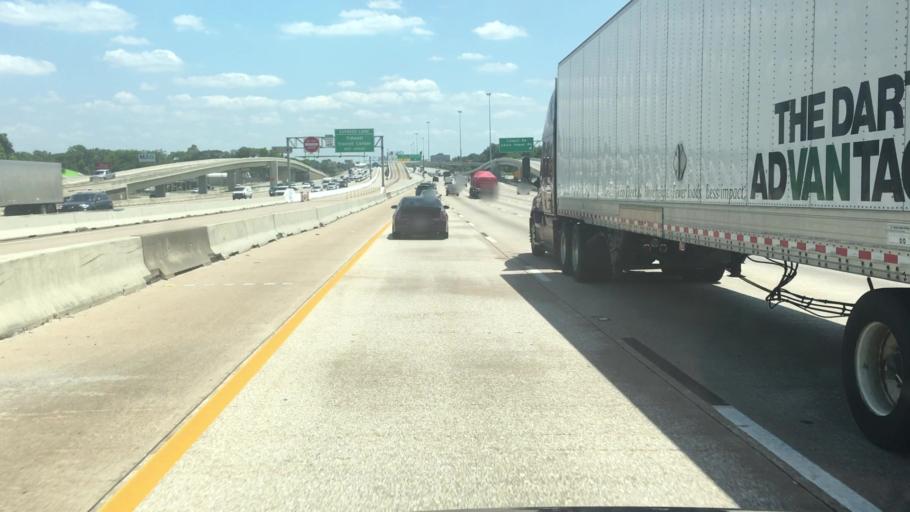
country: US
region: Texas
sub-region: Harris County
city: Aldine
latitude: 29.8574
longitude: -95.3337
